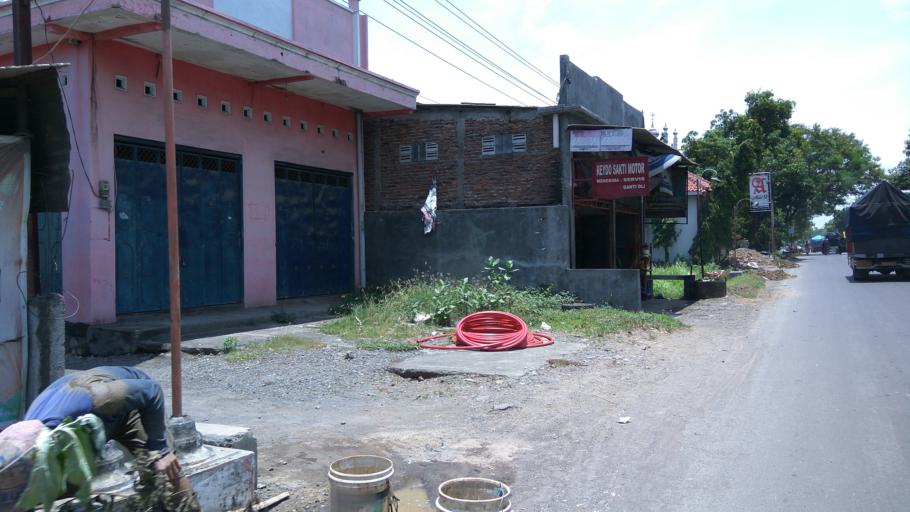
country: ID
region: Central Java
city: Mranggen
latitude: -7.0287
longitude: 110.5301
